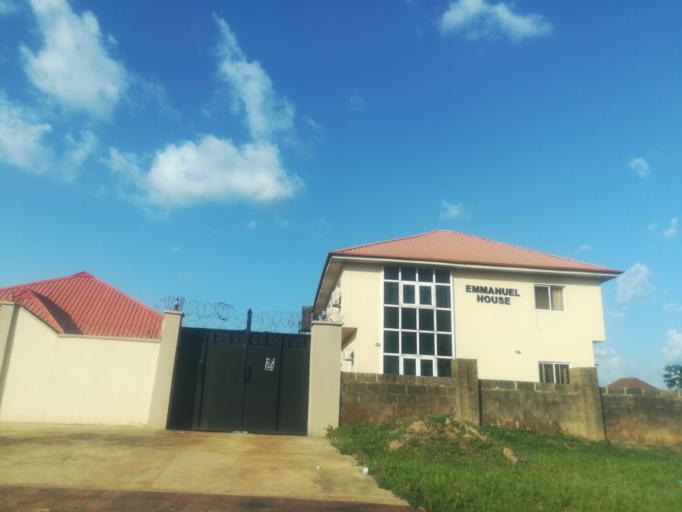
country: NG
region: Oyo
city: Ibadan
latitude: 7.4348
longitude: 3.9740
